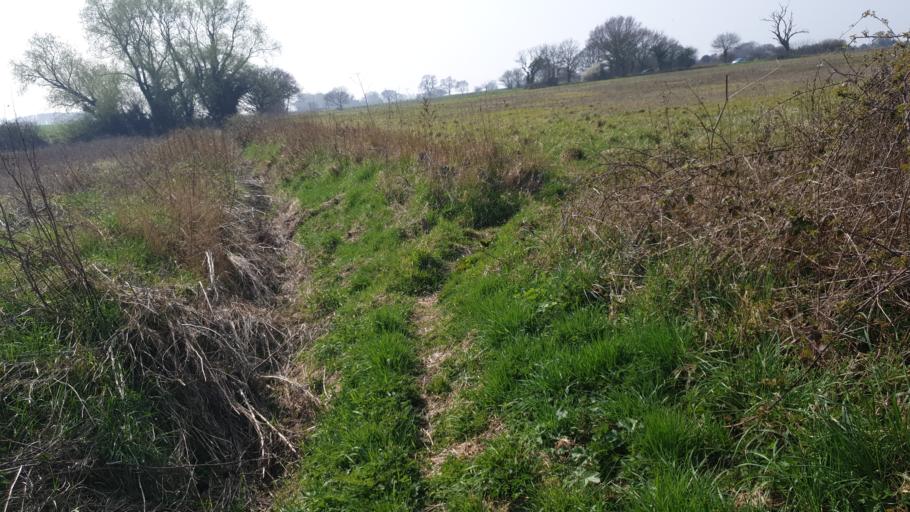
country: GB
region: England
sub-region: Essex
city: Mistley
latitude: 51.9339
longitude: 1.1707
